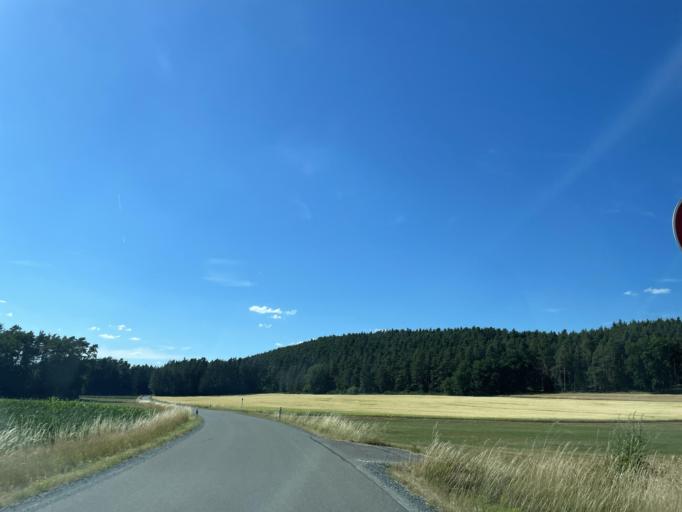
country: DE
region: Bavaria
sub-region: Upper Palatinate
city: Speinshart
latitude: 49.7762
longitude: 11.8593
